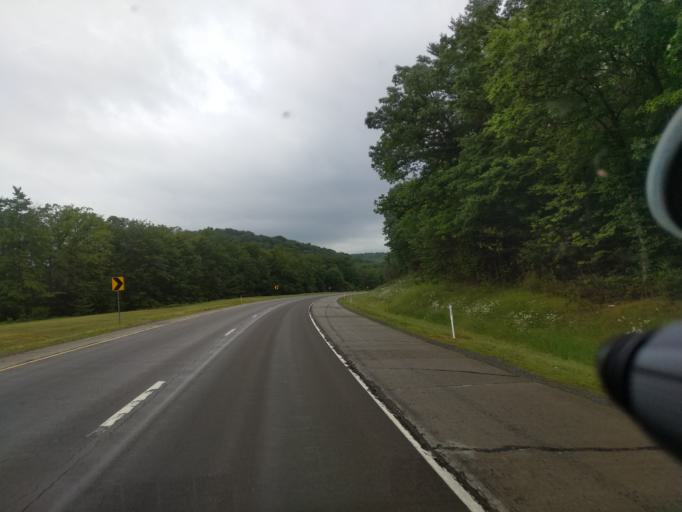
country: US
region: Pennsylvania
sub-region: Union County
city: Mifflinburg
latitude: 41.0412
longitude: -77.1364
